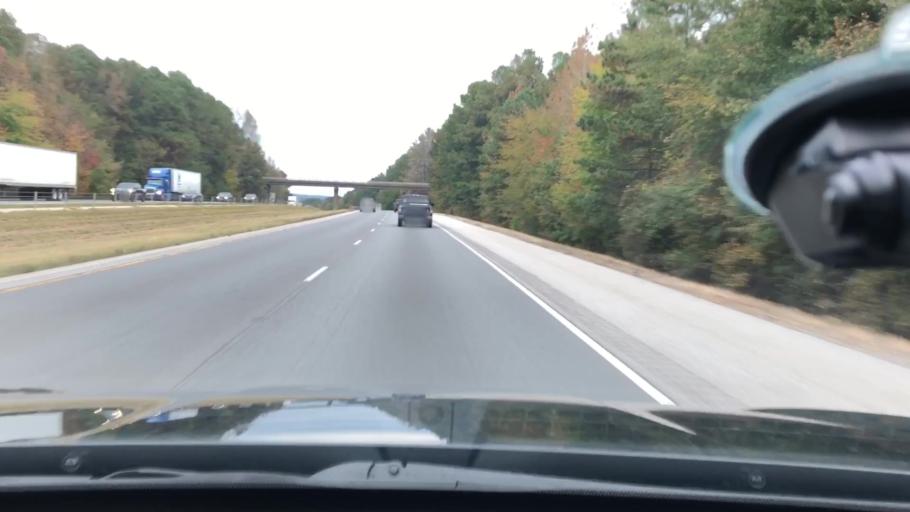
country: US
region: Arkansas
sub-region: Clark County
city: Arkadelphia
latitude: 34.1406
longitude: -93.0811
